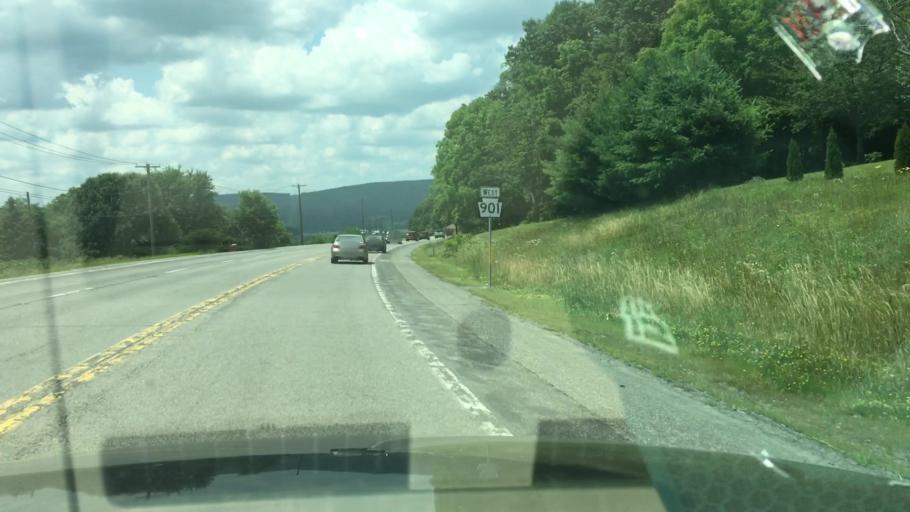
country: US
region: Pennsylvania
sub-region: Schuylkill County
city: Ashland
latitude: 40.7223
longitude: -76.3784
